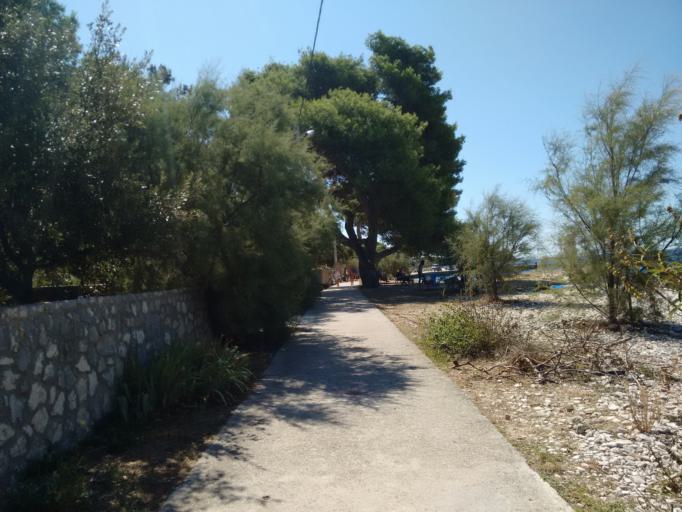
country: HR
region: Licko-Senjska
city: Novalja
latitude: 44.3753
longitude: 14.6916
